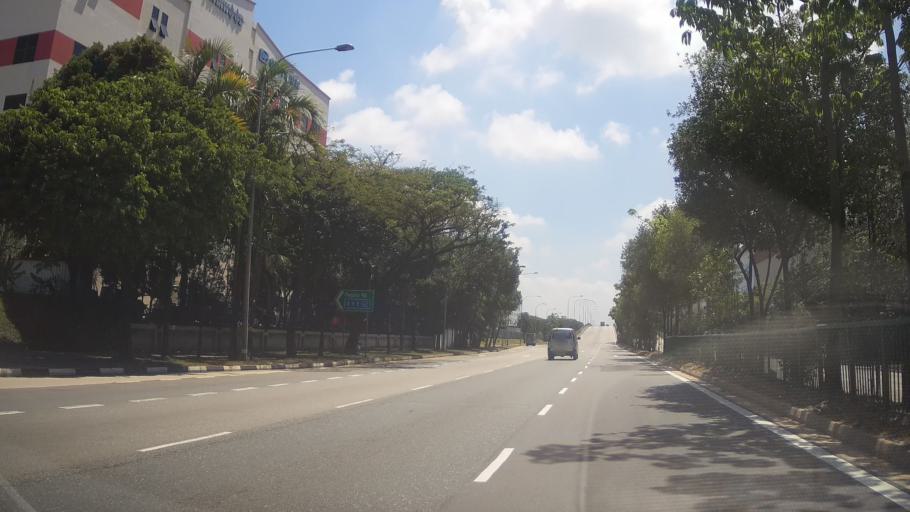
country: SG
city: Singapore
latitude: 1.3121
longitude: 103.7301
